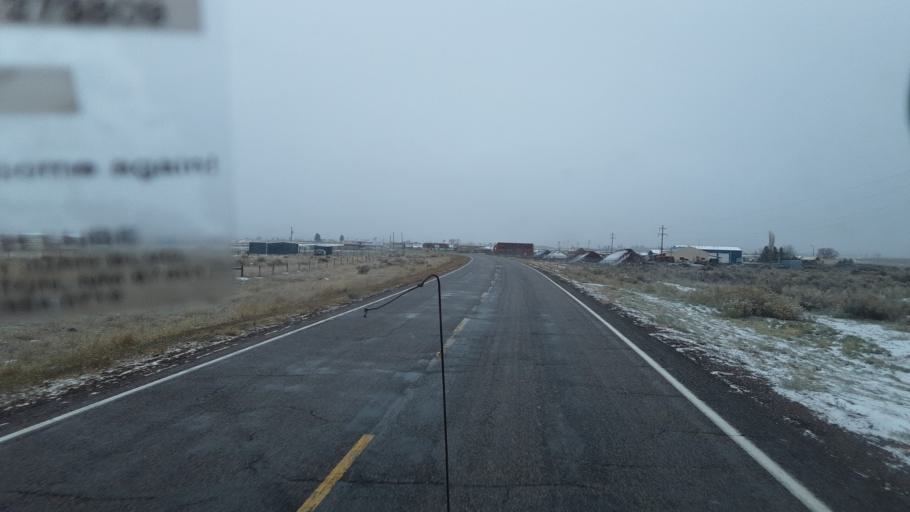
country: US
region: New Mexico
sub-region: Rio Arriba County
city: Tierra Amarilla
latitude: 36.7064
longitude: -106.5580
